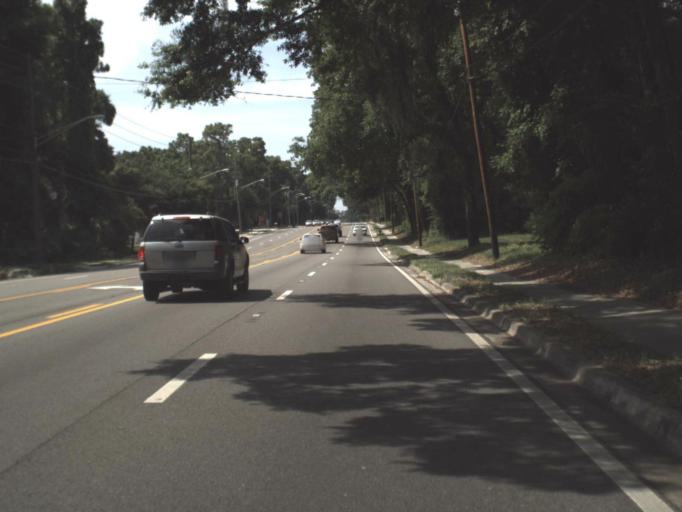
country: US
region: Florida
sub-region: Duval County
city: Jacksonville
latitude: 30.3077
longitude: -81.6004
